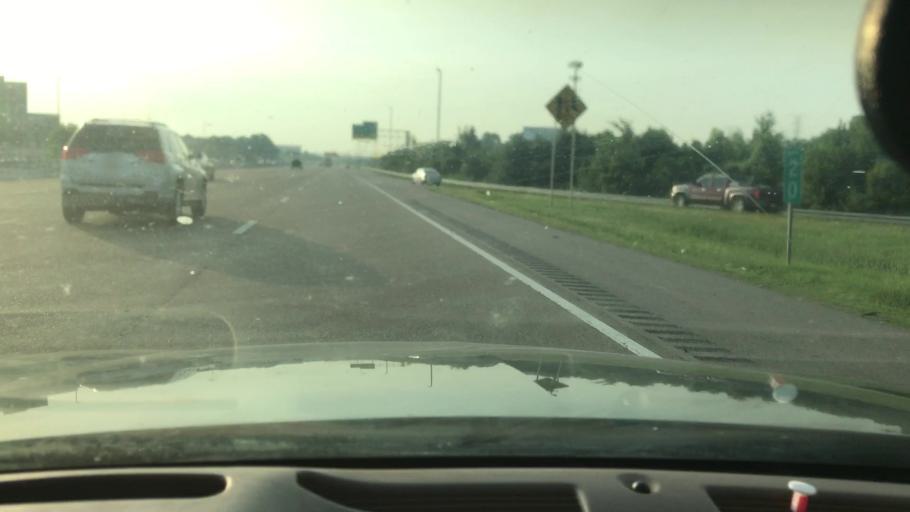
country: US
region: Tennessee
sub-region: Shelby County
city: Germantown
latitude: 35.0795
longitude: -89.9286
